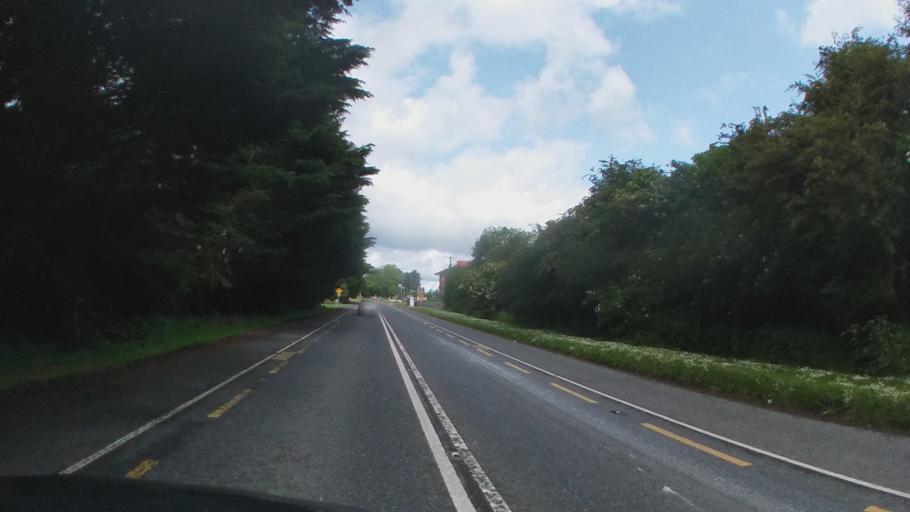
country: IE
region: Leinster
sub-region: Kilkenny
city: Kilkenny
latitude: 52.6472
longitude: -7.2098
